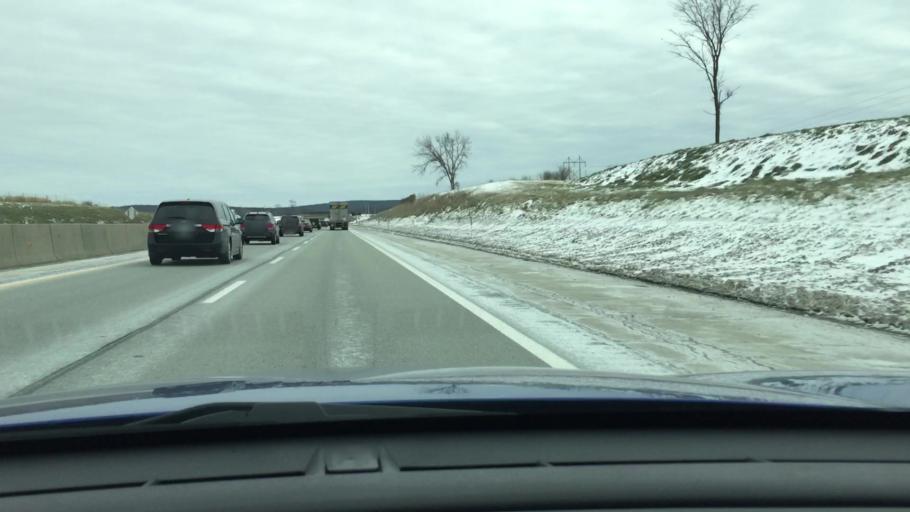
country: US
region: Pennsylvania
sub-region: Somerset County
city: Berlin
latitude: 39.9743
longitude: -78.9120
